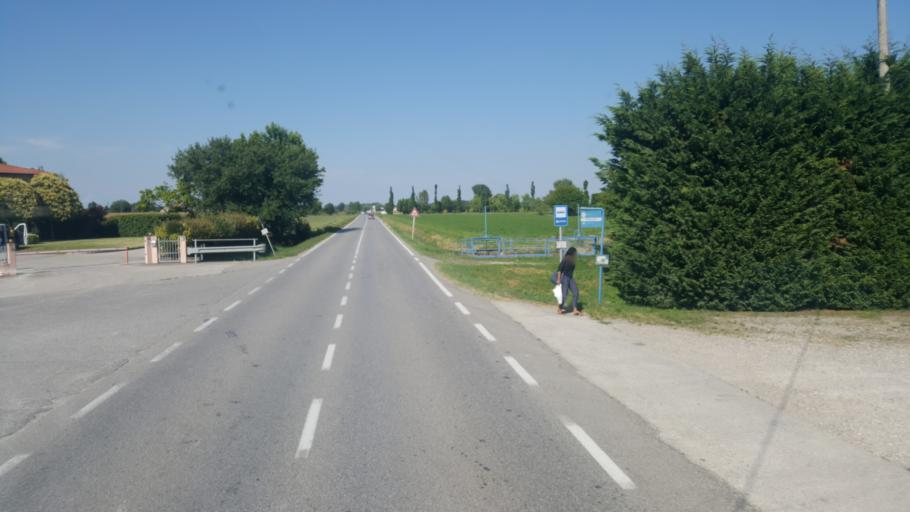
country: IT
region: Lombardy
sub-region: Provincia di Mantova
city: Casalromano
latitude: 45.2046
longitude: 10.3800
